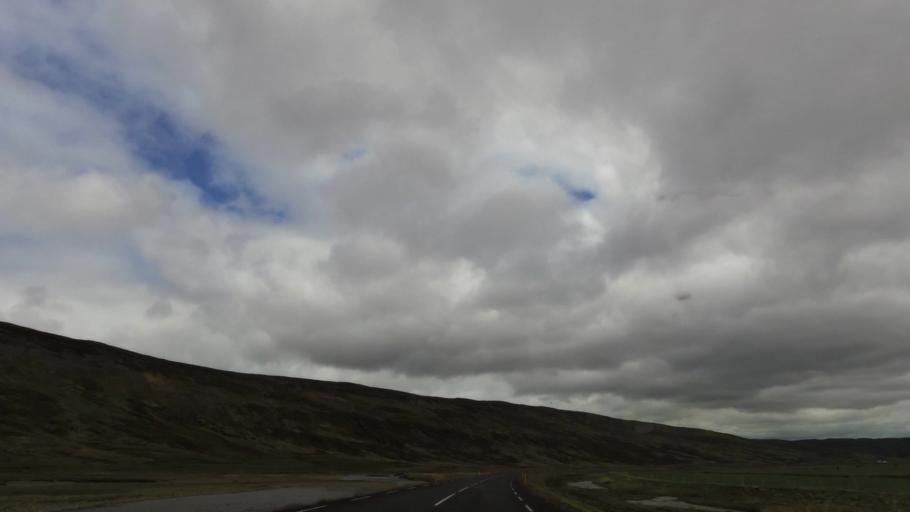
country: IS
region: West
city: Stykkisholmur
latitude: 65.7641
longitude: -21.8375
